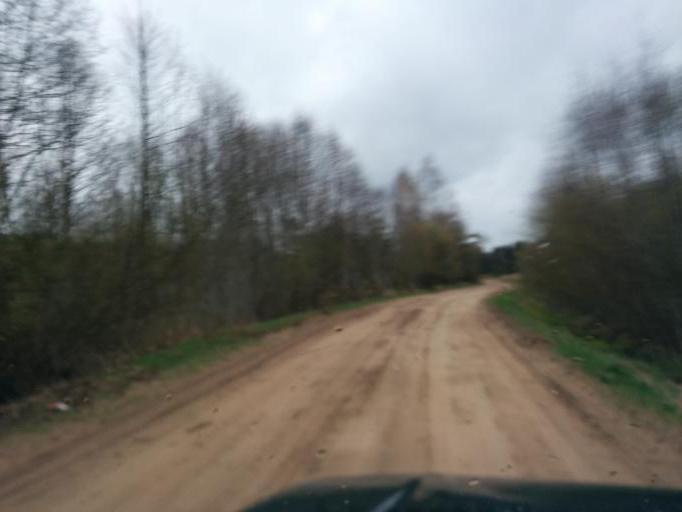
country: LV
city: Tireli
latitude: 56.7867
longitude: 23.6452
